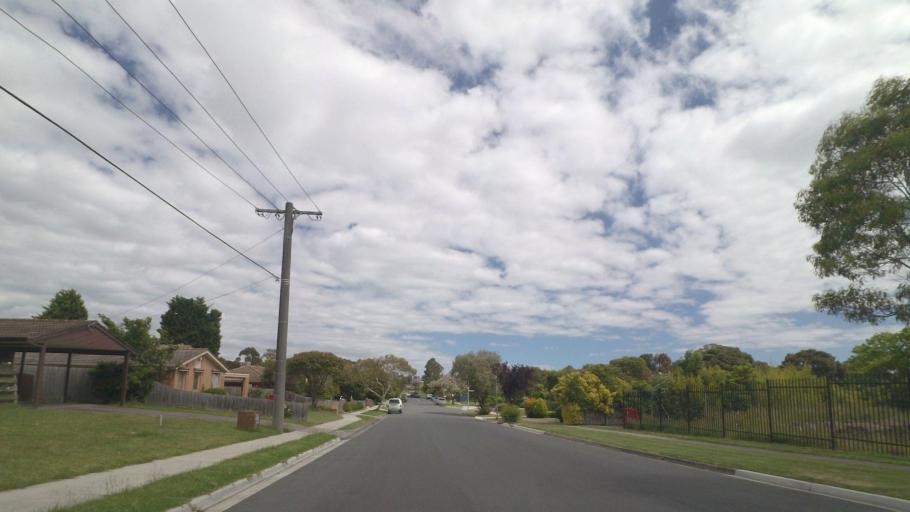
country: AU
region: Victoria
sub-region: Knox
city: Knoxfield
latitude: -37.8743
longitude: 145.2375
